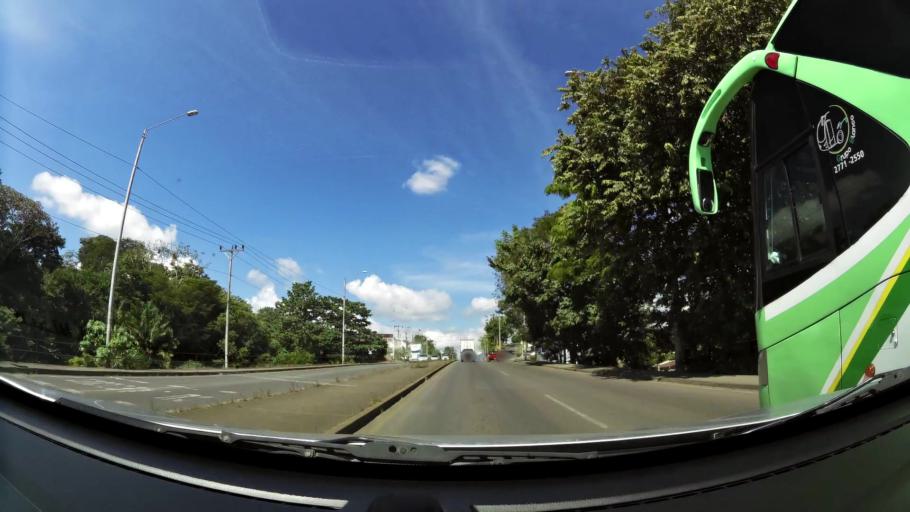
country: CR
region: San Jose
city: San Isidro
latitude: 9.3650
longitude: -83.6947
